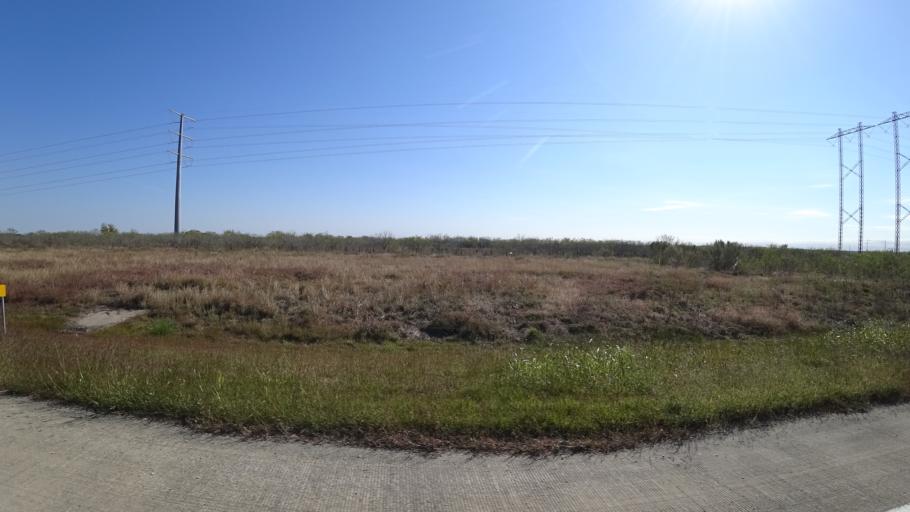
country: US
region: Texas
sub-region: Travis County
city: Onion Creek
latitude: 30.0964
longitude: -97.6739
